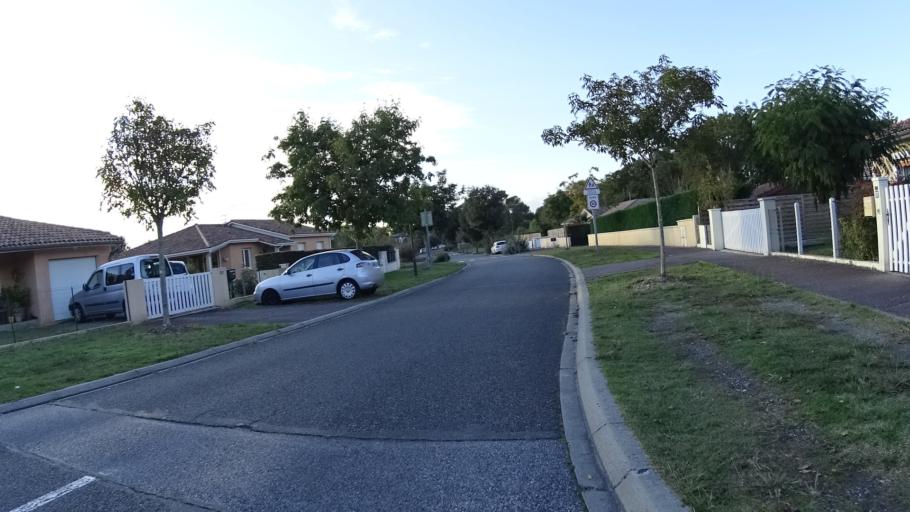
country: FR
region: Aquitaine
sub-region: Departement des Landes
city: Saint-Paul-les-Dax
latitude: 43.7358
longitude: -1.0459
